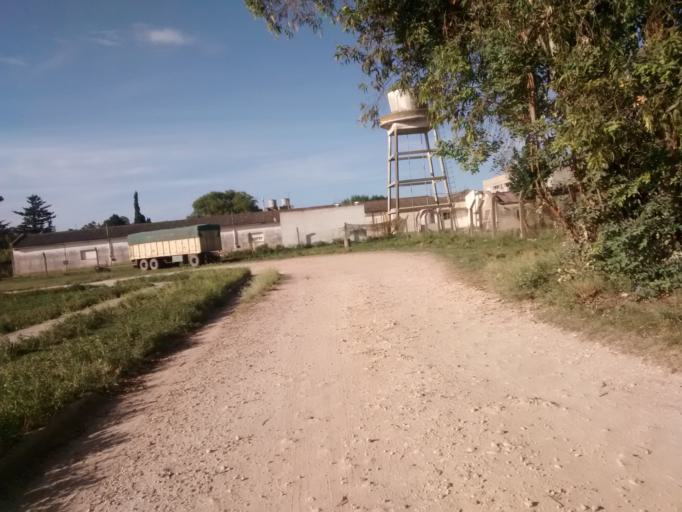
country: AR
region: Buenos Aires
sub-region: Partido de Loberia
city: Loberia
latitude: -38.1726
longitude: -58.7740
